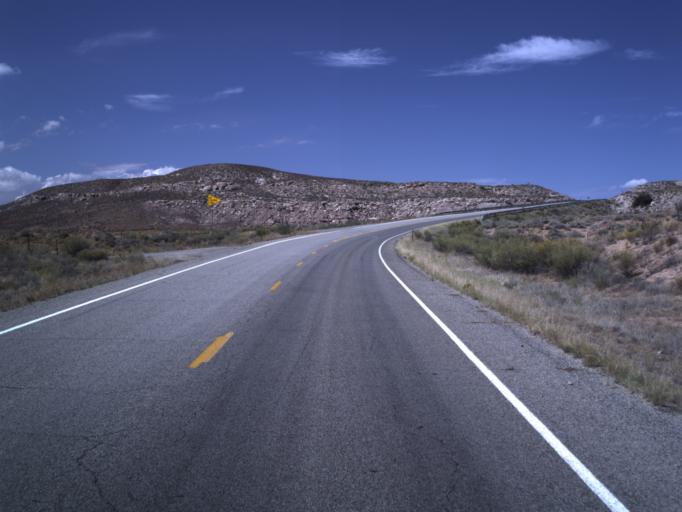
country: US
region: Utah
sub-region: San Juan County
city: Blanding
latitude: 37.2732
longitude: -109.3436
